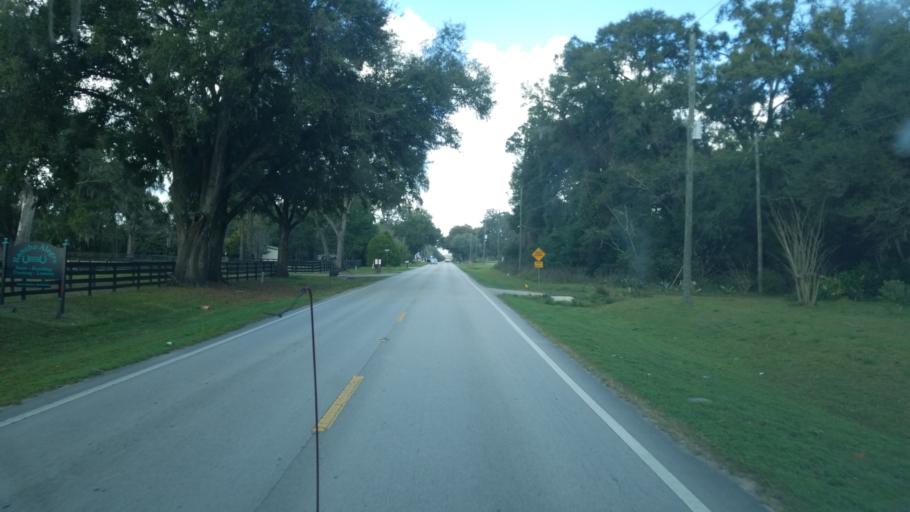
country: US
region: Florida
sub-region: Marion County
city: Ocala
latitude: 29.0870
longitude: -82.1691
